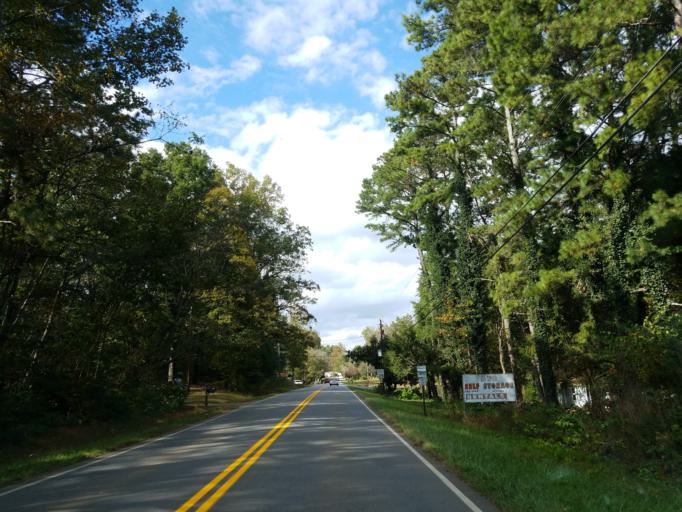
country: US
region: Georgia
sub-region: Pickens County
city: Jasper
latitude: 34.4336
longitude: -84.4215
